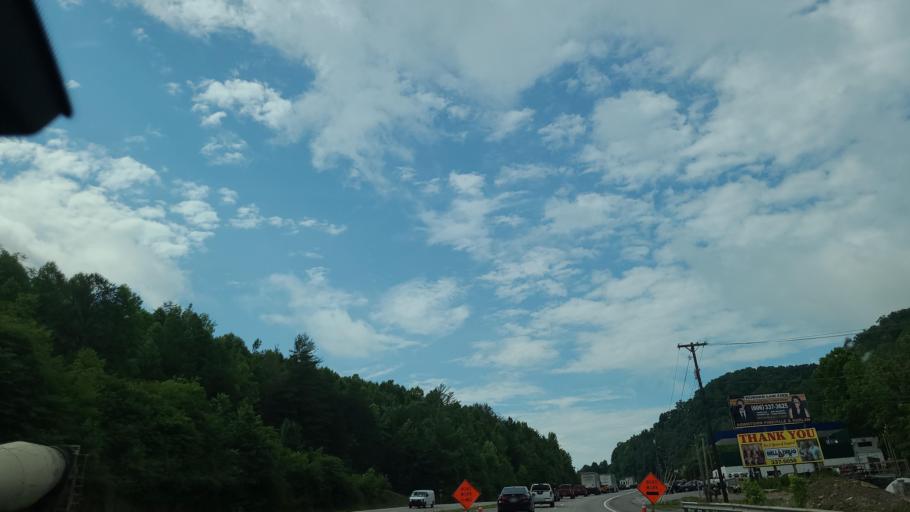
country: US
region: Kentucky
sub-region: Bell County
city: Pineville
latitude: 36.7265
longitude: -83.6901
